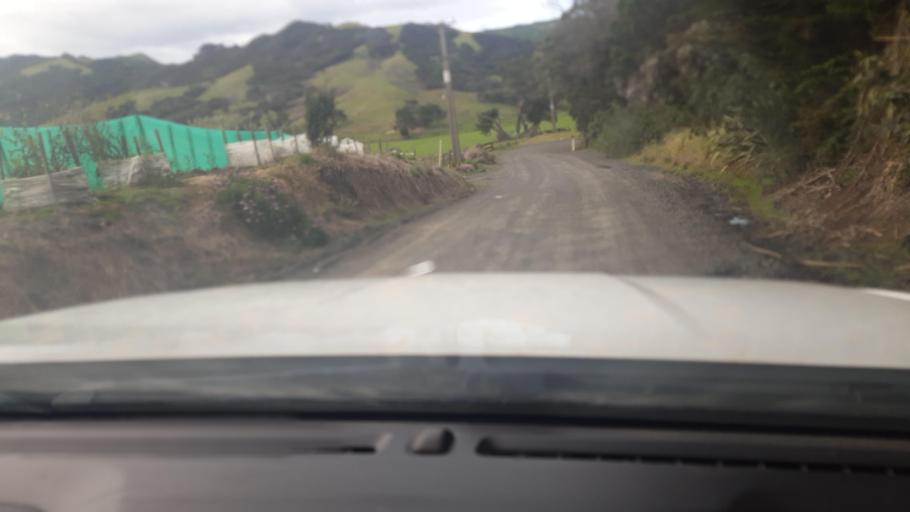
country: NZ
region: Northland
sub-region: Far North District
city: Ahipara
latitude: -35.2847
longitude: 173.2066
